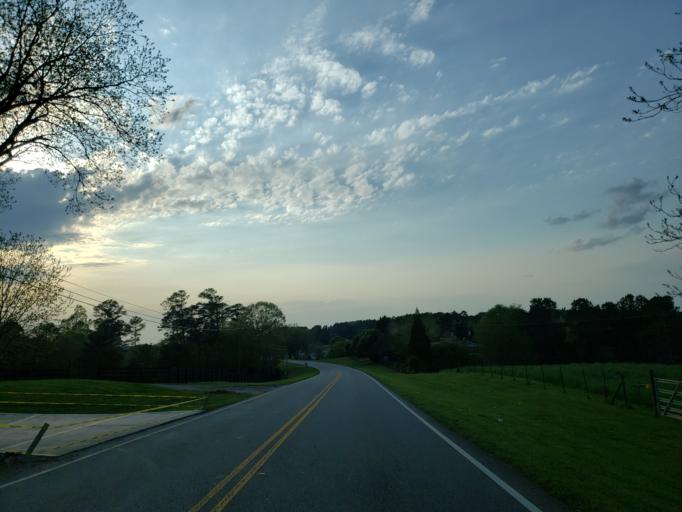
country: US
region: Georgia
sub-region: Cherokee County
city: Ball Ground
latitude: 34.2662
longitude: -84.3623
